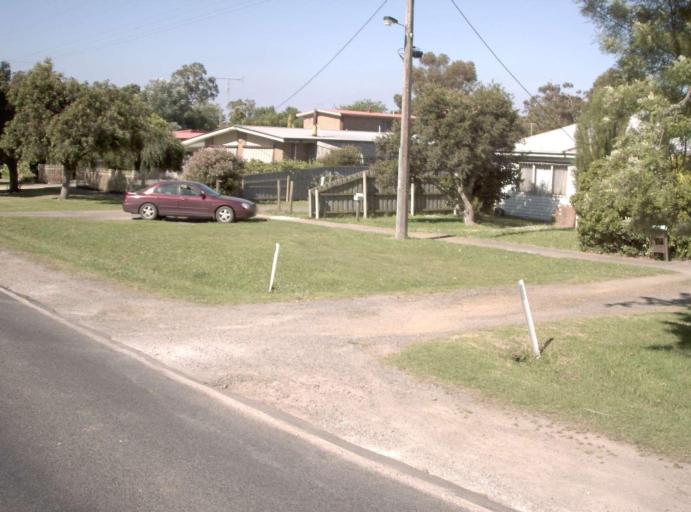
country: AU
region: Victoria
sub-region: Latrobe
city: Traralgon
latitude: -38.5709
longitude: 146.6743
